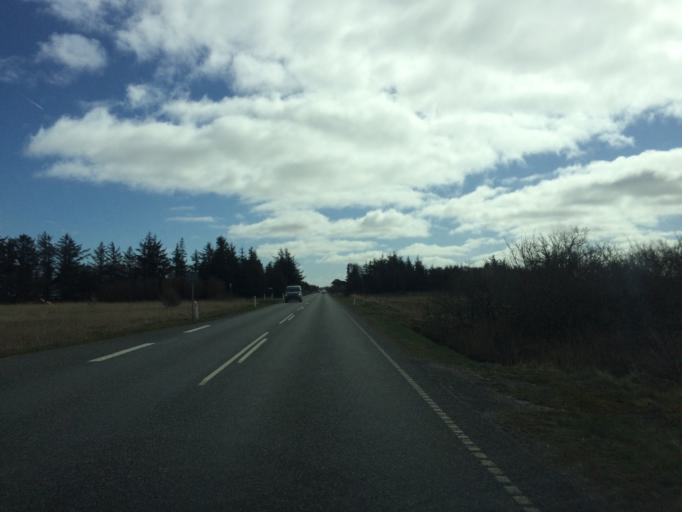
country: DK
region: Central Jutland
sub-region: Holstebro Kommune
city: Ulfborg
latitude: 56.3164
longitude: 8.1635
